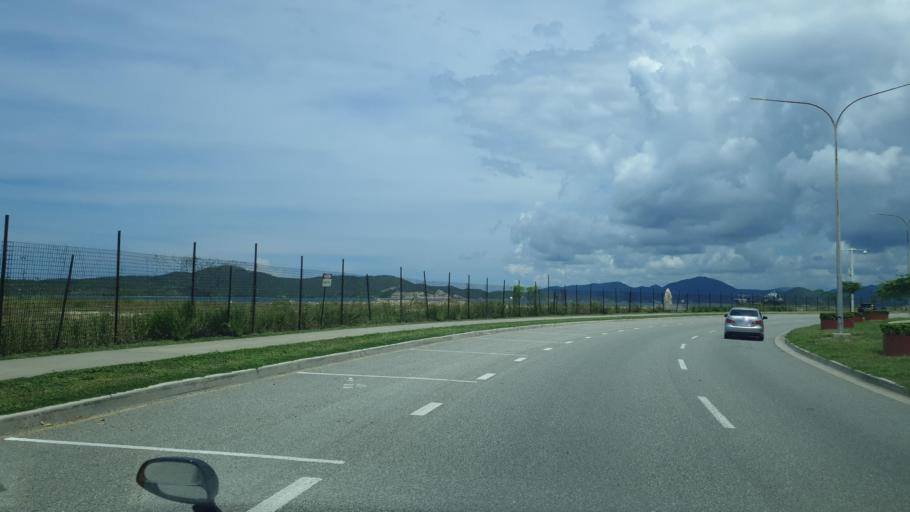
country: PG
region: National Capital
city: Port Moresby
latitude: -9.4850
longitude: 147.1437
